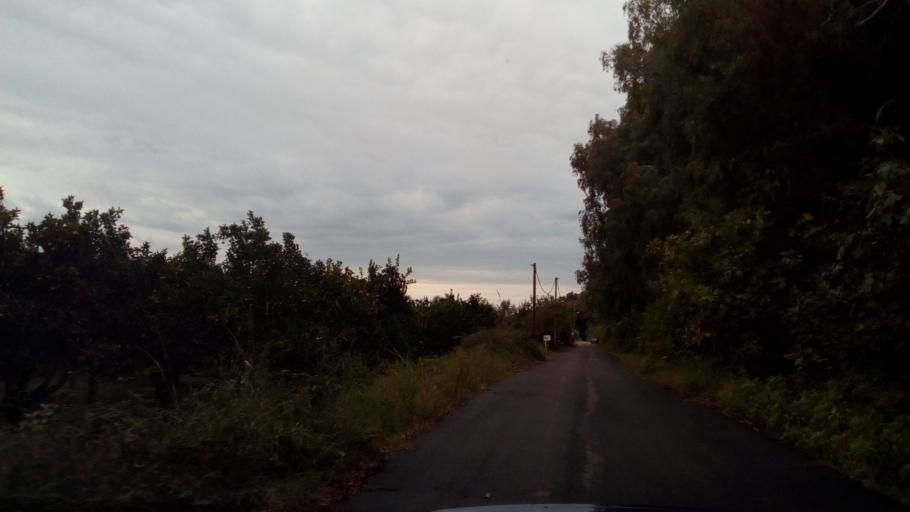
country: GR
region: West Greece
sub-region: Nomos Aitolias kai Akarnanias
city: Nafpaktos
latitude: 38.3971
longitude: 21.8689
